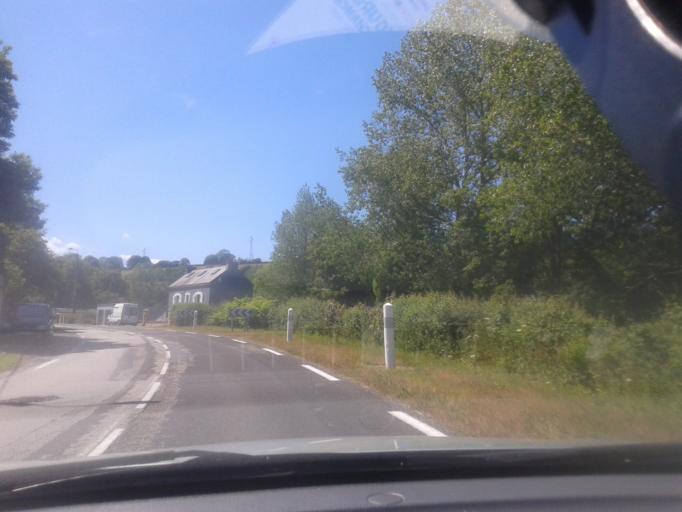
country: FR
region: Lower Normandy
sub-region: Departement de la Manche
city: Octeville
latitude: 49.6155
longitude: -1.6409
